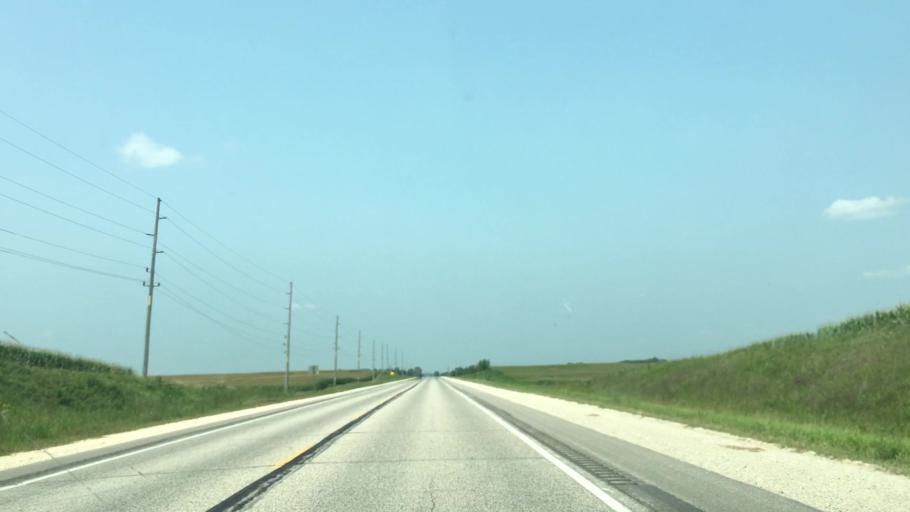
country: US
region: Iowa
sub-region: Fayette County
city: Fayette
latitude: 42.8851
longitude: -91.8105
